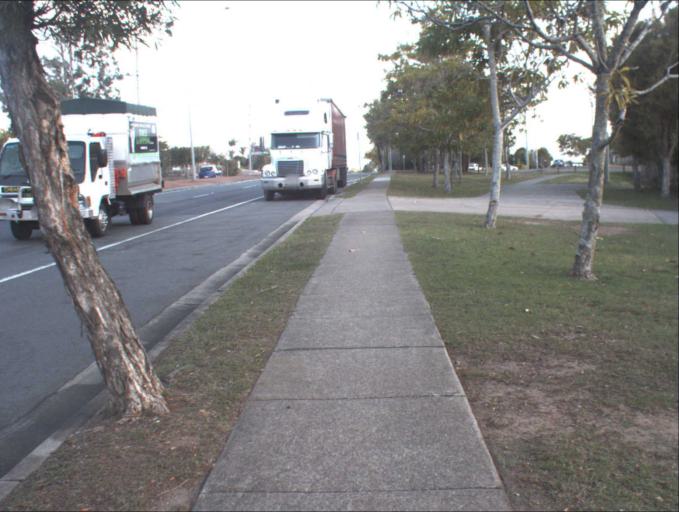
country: AU
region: Queensland
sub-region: Logan
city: Waterford West
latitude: -27.6804
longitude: 153.1215
